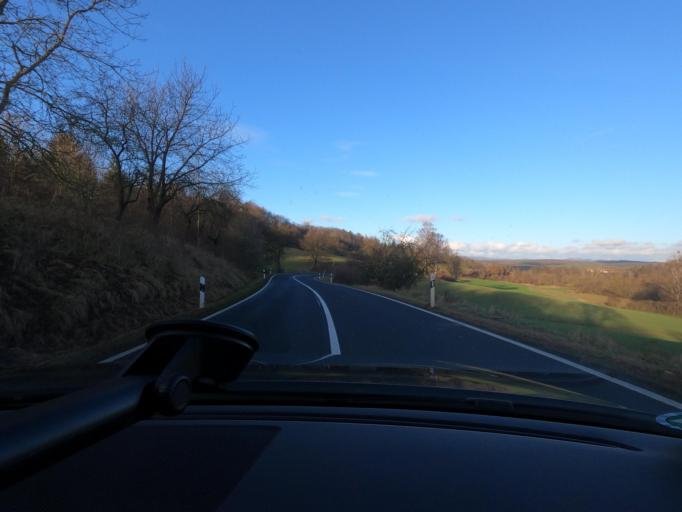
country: DE
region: Lower Saxony
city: Rhumspringe
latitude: 51.5515
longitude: 10.3042
